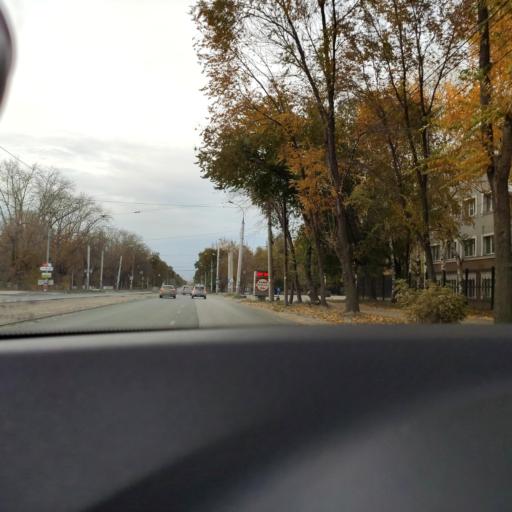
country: RU
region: Samara
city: Smyshlyayevka
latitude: 53.1949
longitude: 50.2916
